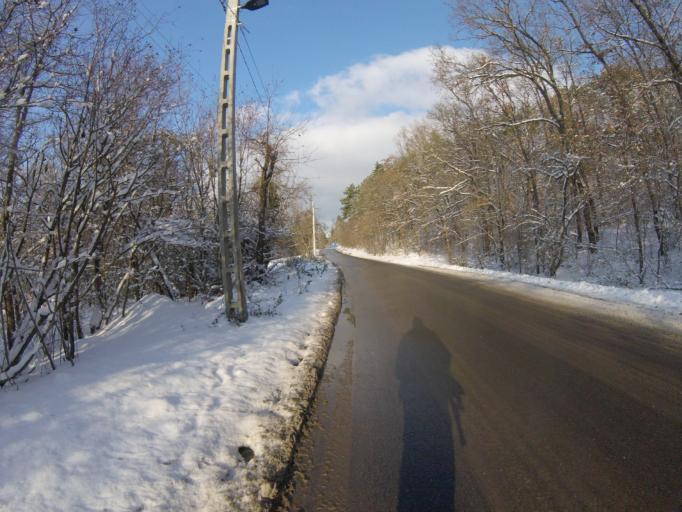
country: HU
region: Pest
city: Budakeszi
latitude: 47.5017
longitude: 18.9231
